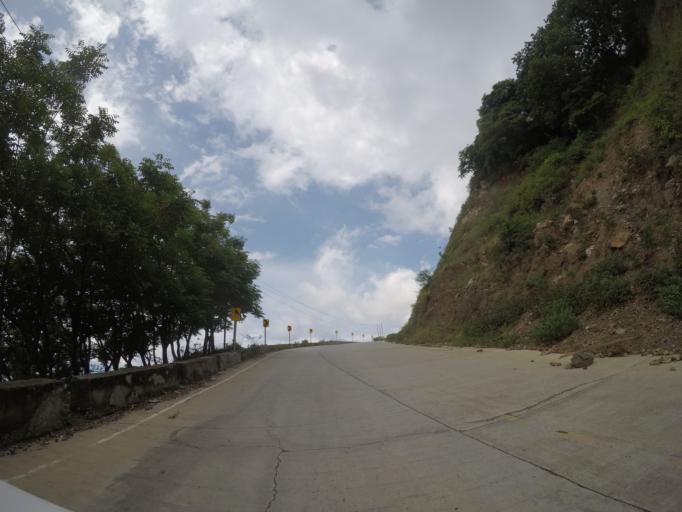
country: TL
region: Liquica
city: Maubara
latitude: -8.6660
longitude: 125.1107
